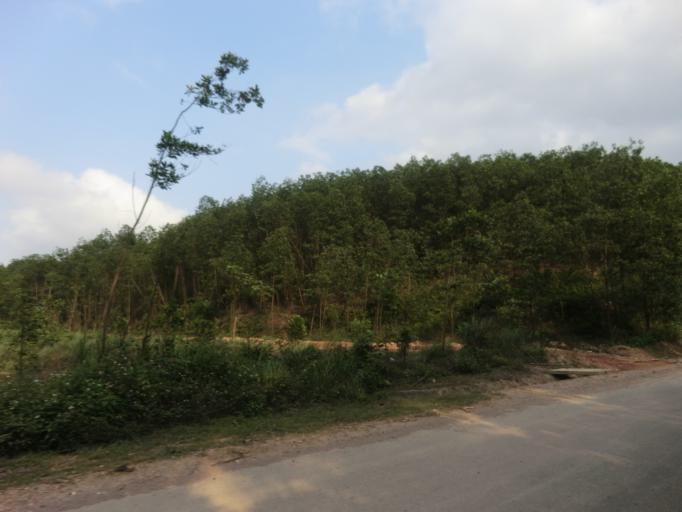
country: VN
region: Quang Binh
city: Kien Giang
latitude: 17.0983
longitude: 106.8473
